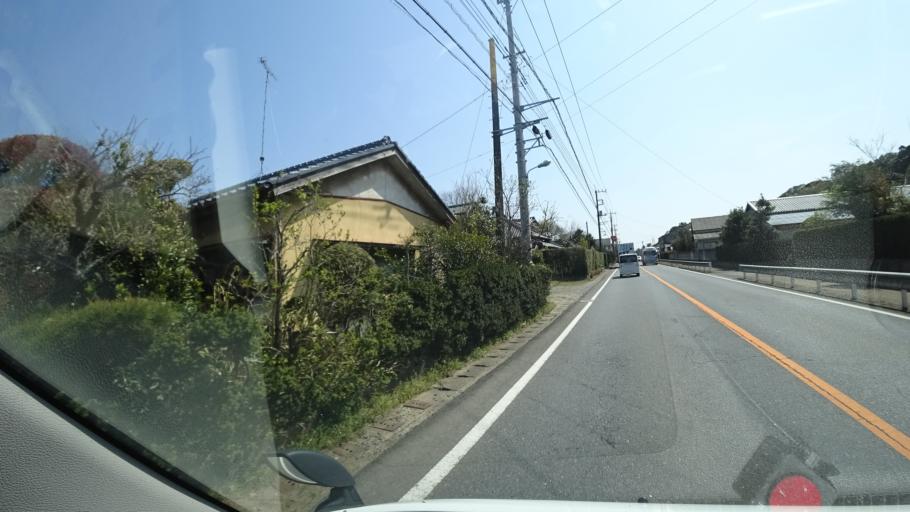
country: JP
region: Chiba
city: Narita
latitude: 35.8618
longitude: 140.2866
